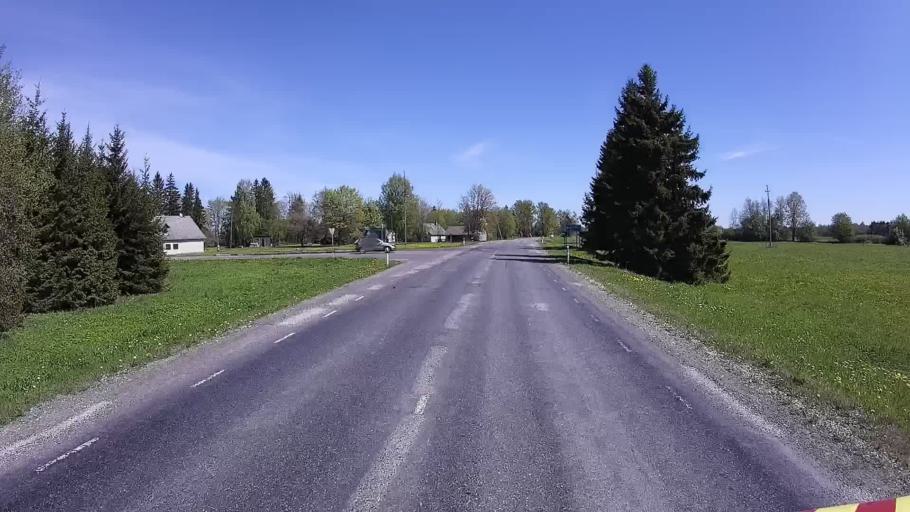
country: EE
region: Raplamaa
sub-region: Kehtna vald
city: Kehtna
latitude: 59.0553
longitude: 24.9769
